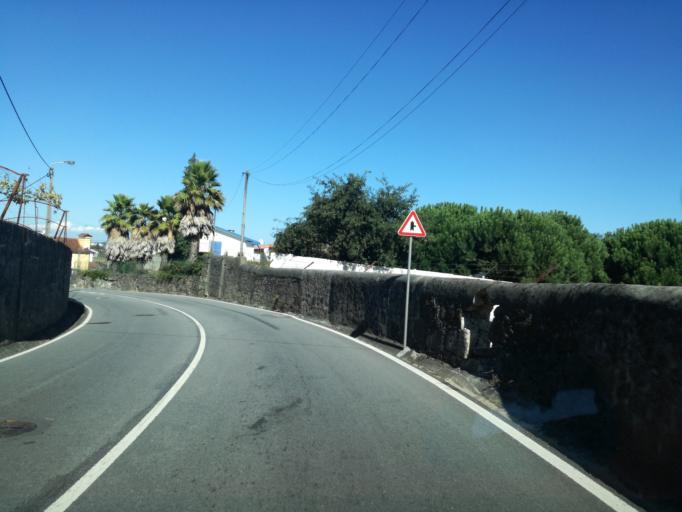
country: PT
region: Porto
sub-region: Trofa
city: Sao Romao do Coronado
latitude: 41.2831
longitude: -8.5797
